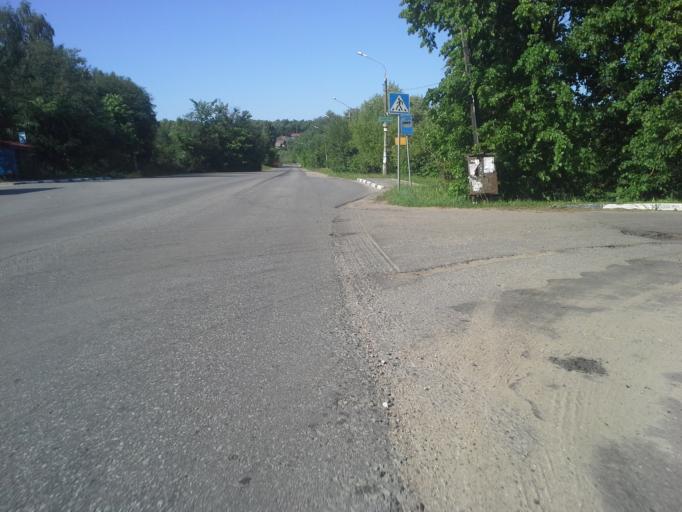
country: RU
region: Moskovskaya
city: Dubrovitsy
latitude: 55.4432
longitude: 37.3996
